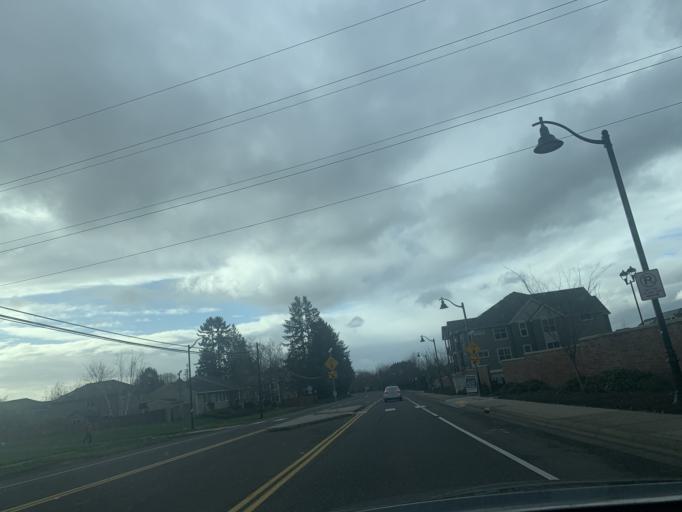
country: US
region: Oregon
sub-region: Washington County
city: Oak Hills
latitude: 45.5651
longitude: -122.8439
